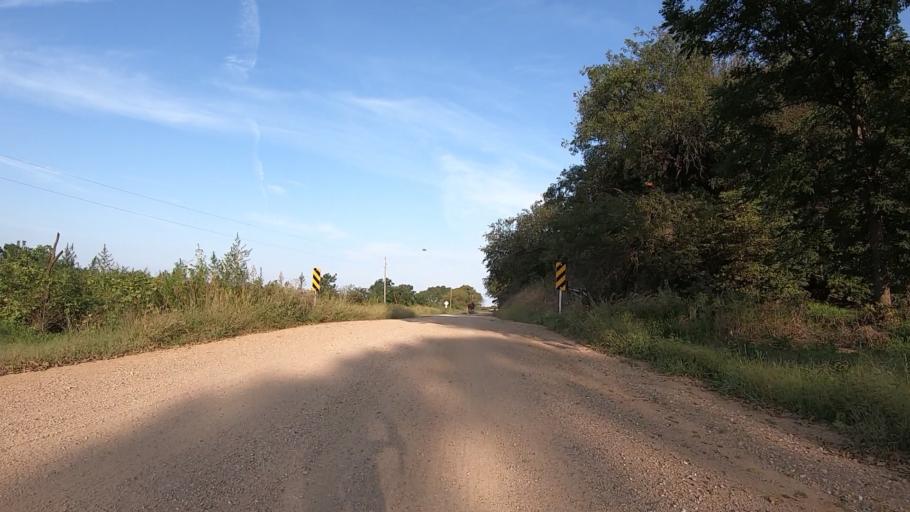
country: US
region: Kansas
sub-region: Marshall County
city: Blue Rapids
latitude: 39.7232
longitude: -96.7802
